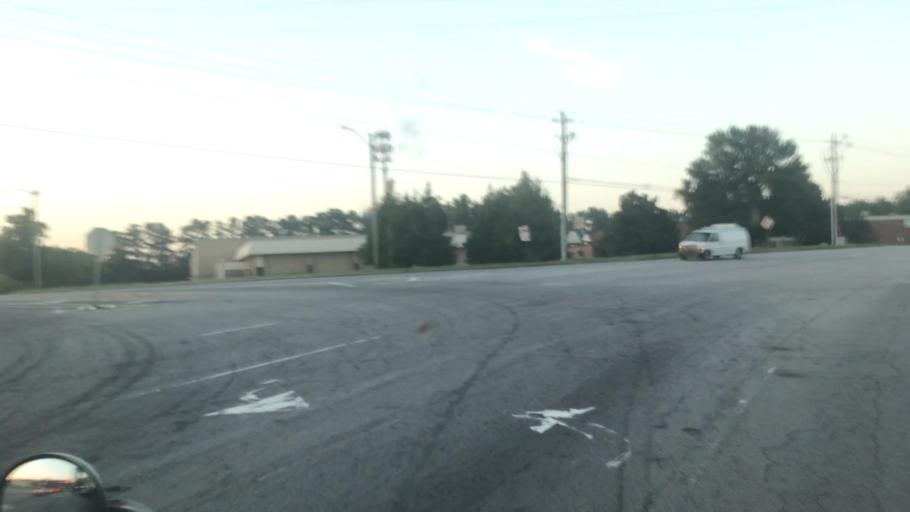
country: US
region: Georgia
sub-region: DeKalb County
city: Doraville
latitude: 33.9301
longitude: -84.2648
